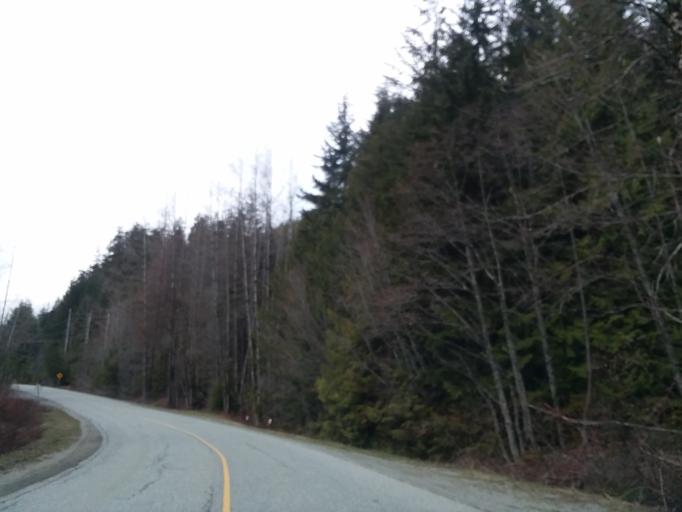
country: CA
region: British Columbia
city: Whistler
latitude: 50.0949
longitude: -123.0093
